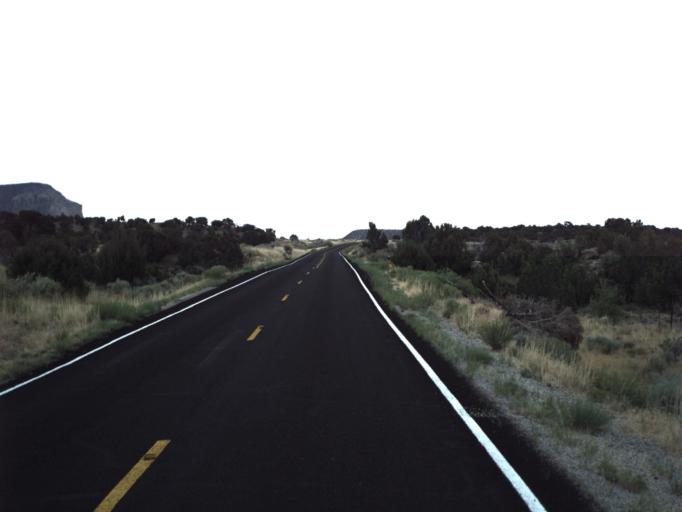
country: US
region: Utah
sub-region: Carbon County
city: East Carbon City
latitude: 39.4792
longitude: -110.4000
